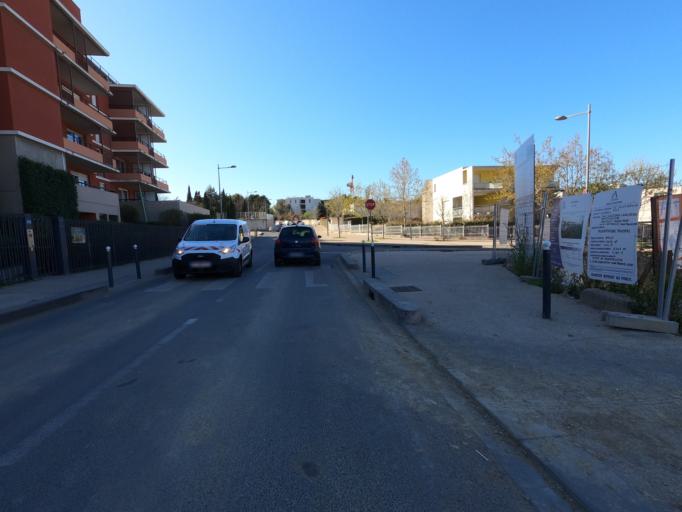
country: FR
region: Languedoc-Roussillon
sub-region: Departement de l'Herault
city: Montpellier
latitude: 43.5840
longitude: 3.8656
